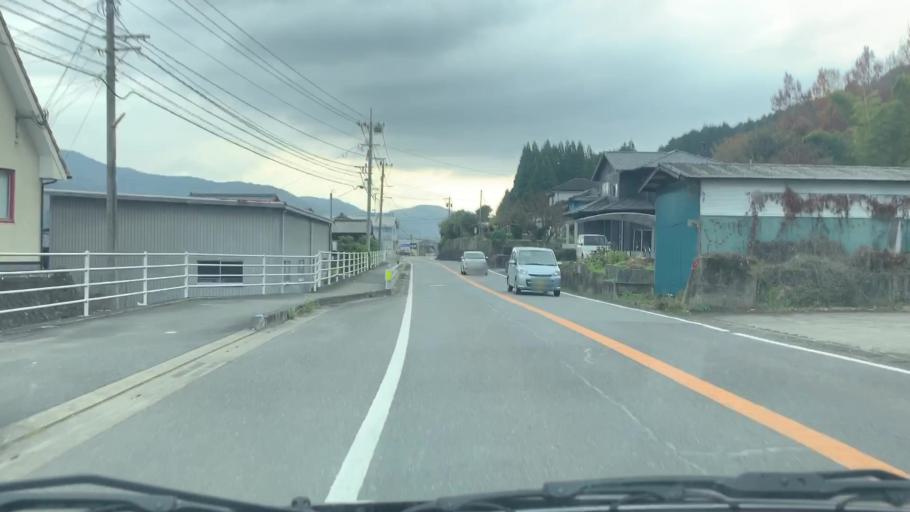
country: JP
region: Saga Prefecture
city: Takeocho-takeo
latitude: 33.1832
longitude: 130.0404
